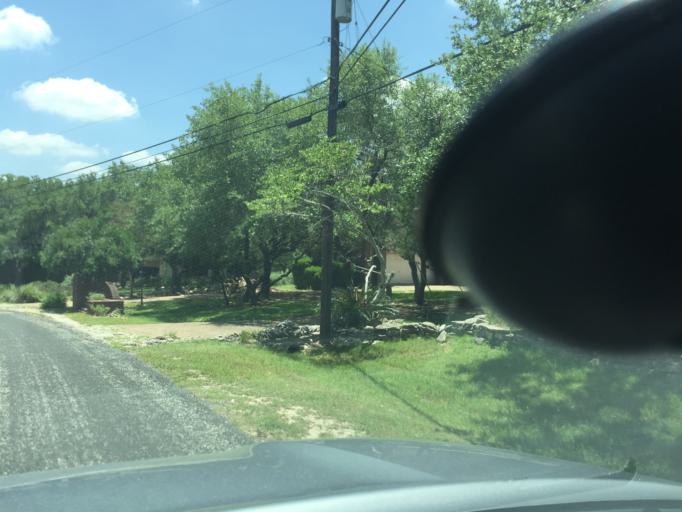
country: US
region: Texas
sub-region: Bexar County
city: Timberwood Park
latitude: 29.6965
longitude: -98.5059
